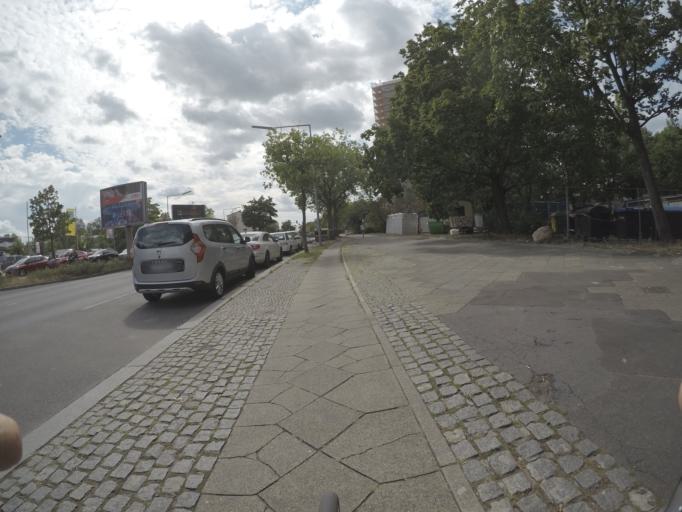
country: DE
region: Berlin
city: Buckow
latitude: 52.4277
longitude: 13.4483
